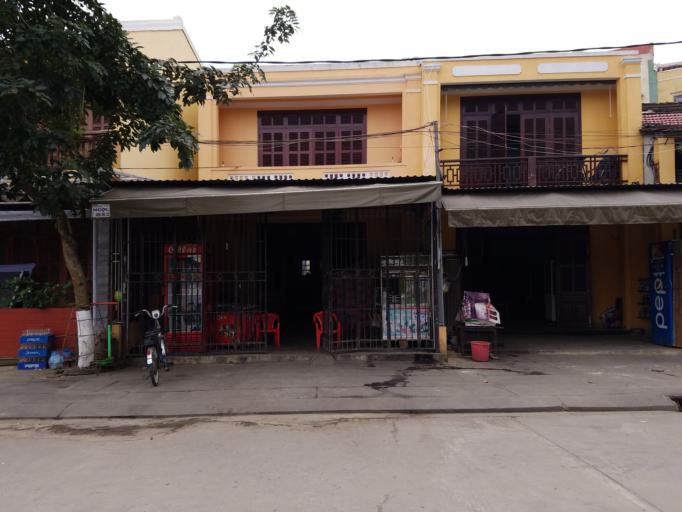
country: VN
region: Quang Nam
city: Hoi An
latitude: 15.8761
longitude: 108.3239
